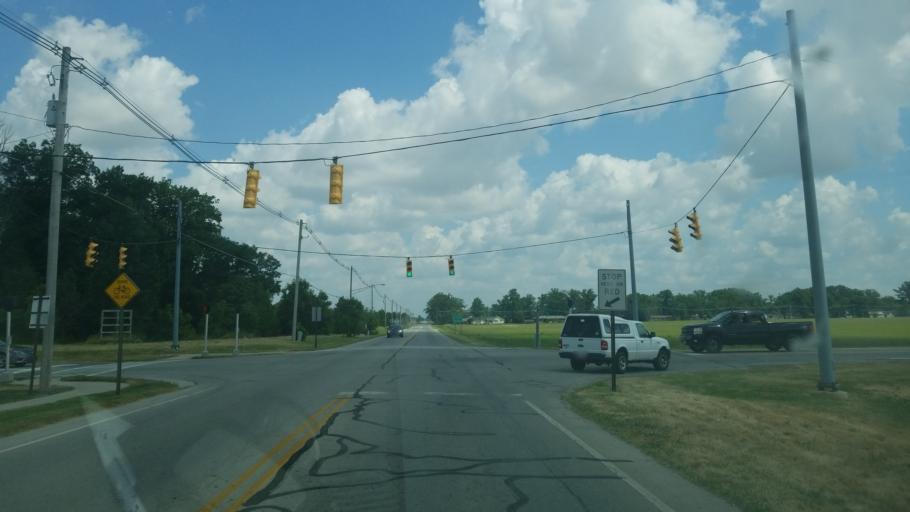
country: US
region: Ohio
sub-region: Auglaize County
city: Wapakoneta
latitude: 40.5851
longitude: -84.2028
